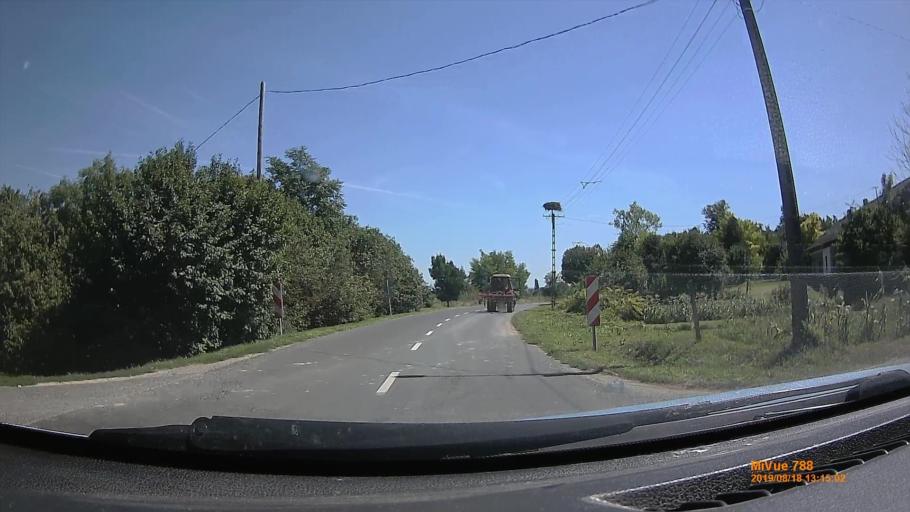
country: HU
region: Fejer
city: Sarbogard
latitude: 46.8718
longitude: 18.5426
